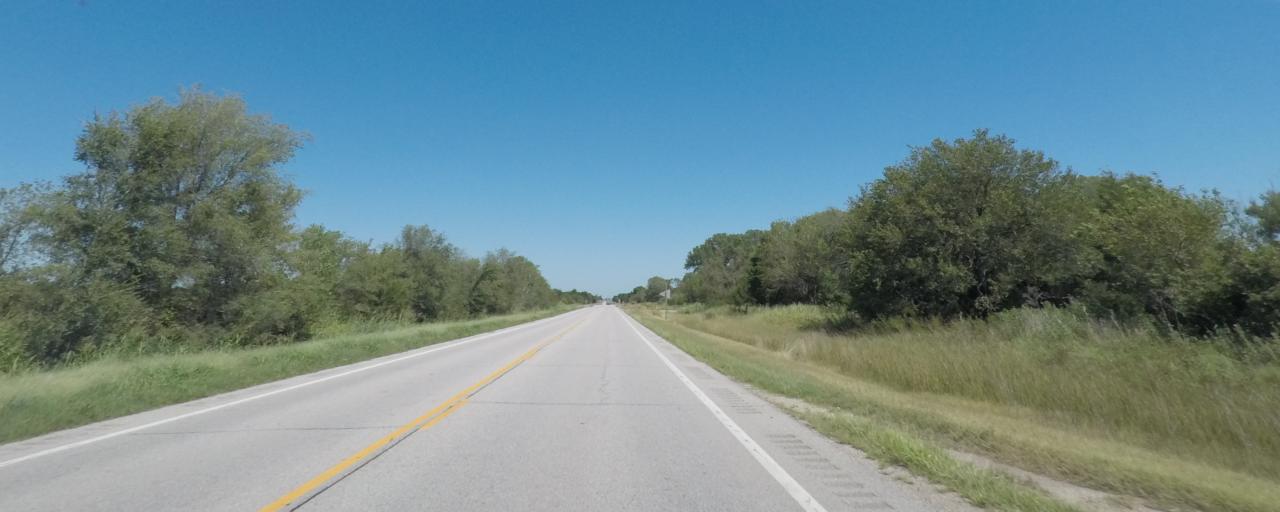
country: US
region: Kansas
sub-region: Sumner County
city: Belle Plaine
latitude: 37.3738
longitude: -97.3850
